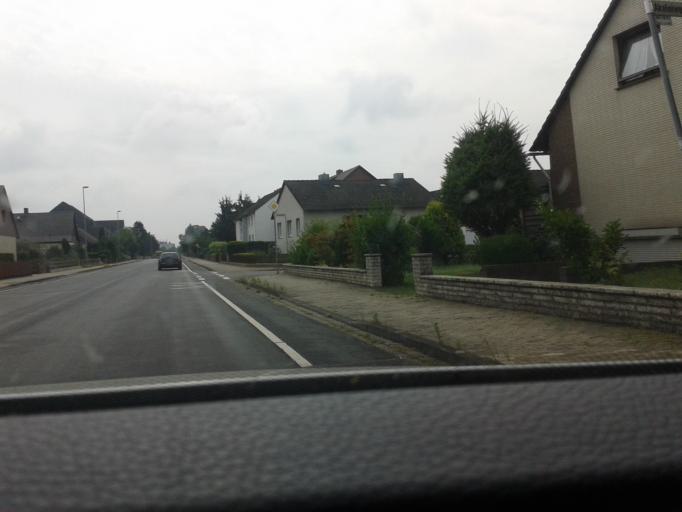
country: DE
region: Lower Saxony
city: Gifhorn
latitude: 52.4843
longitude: 10.5666
